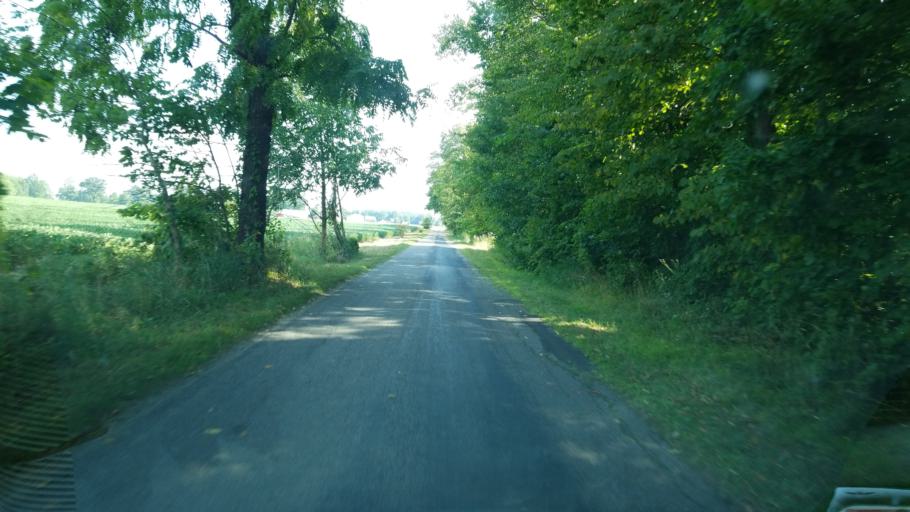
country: US
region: Ohio
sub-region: Union County
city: Richwood
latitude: 40.5194
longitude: -83.2638
